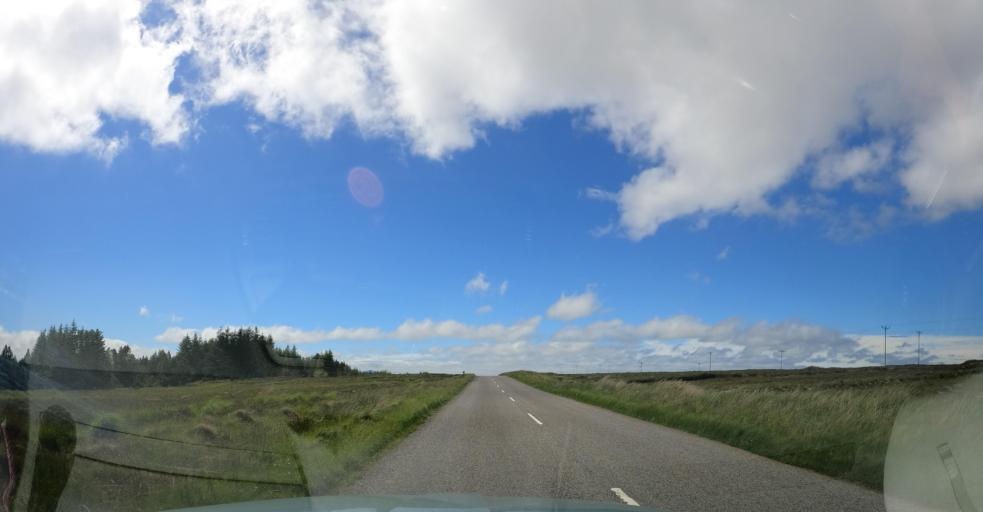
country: GB
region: Scotland
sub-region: Eilean Siar
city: Isle of Lewis
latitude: 58.1797
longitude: -6.6494
